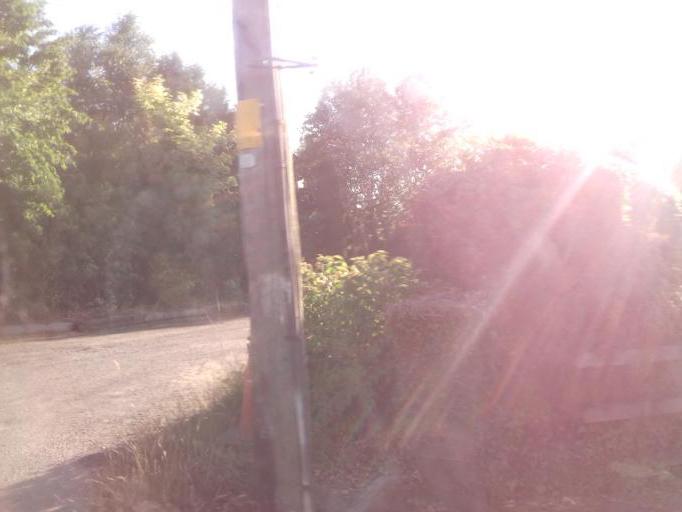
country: IE
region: Leinster
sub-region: Fingal County
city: Swords
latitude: 53.4827
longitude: -6.2975
